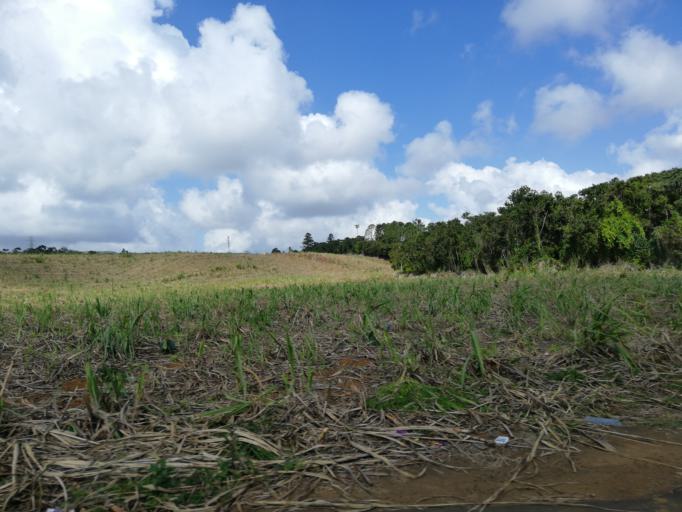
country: MU
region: Pamplemousses
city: Creve Coeur
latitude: -20.2051
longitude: 57.5589
